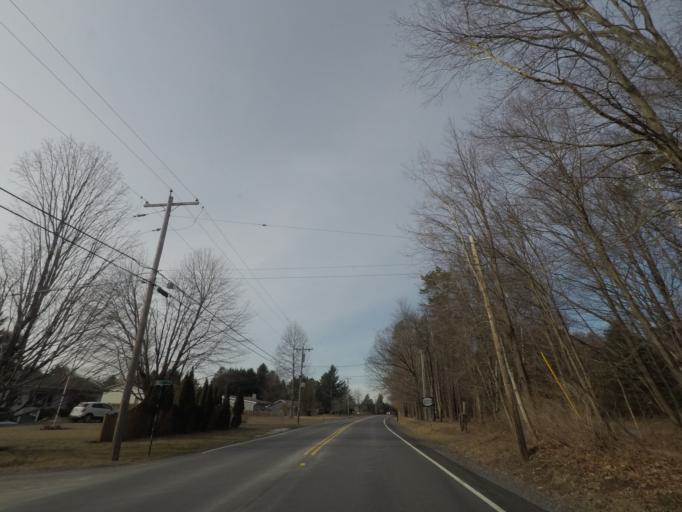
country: US
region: New York
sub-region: Columbia County
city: Valatie
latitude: 42.4036
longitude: -73.6728
